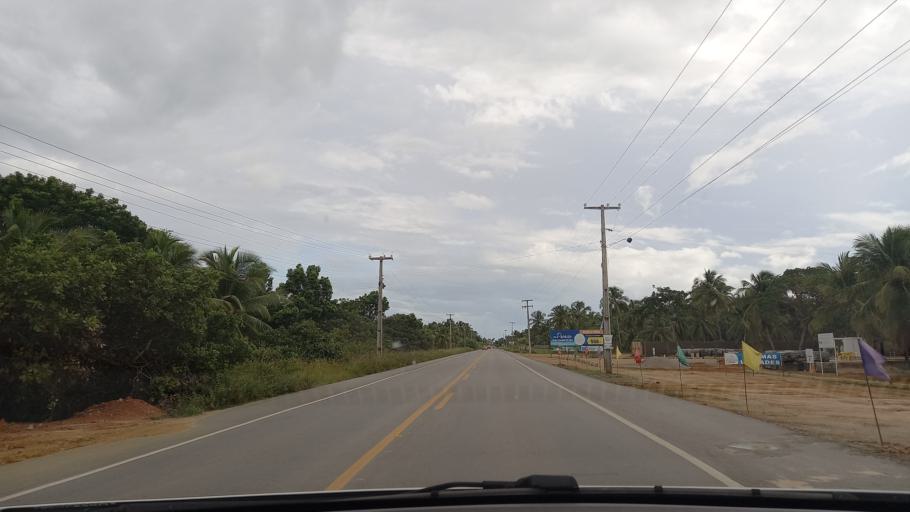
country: BR
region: Alagoas
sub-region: Maragogi
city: Maragogi
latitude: -8.9607
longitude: -35.1800
